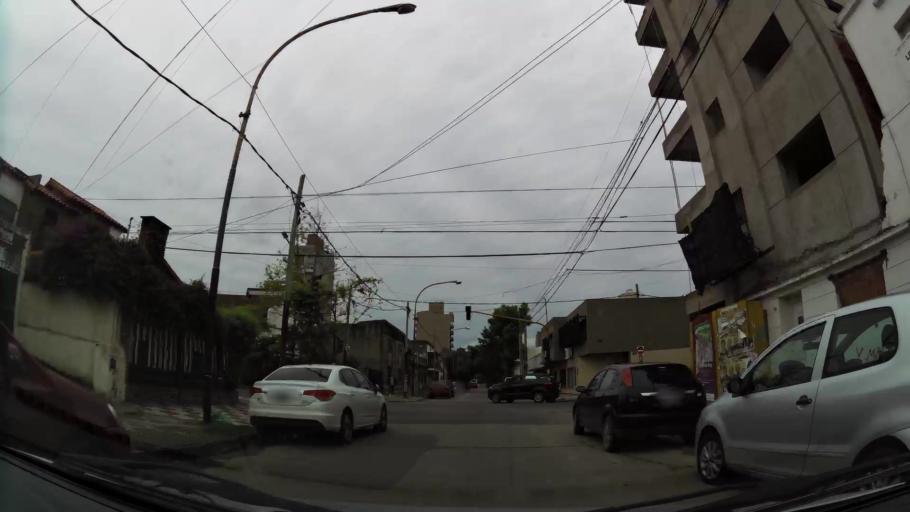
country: AR
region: Buenos Aires
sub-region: Partido de Lanus
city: Lanus
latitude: -34.7104
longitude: -58.3832
